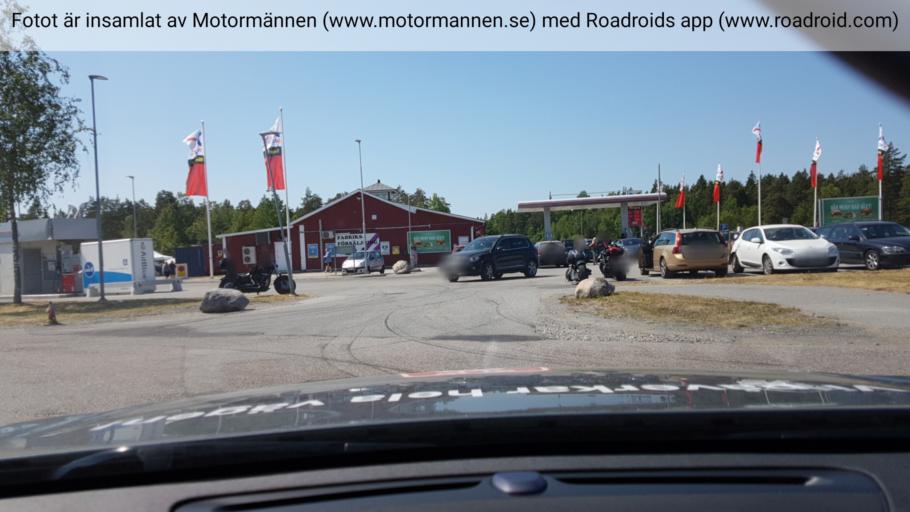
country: SE
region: Stockholm
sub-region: Norrtalje Kommun
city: Rimbo
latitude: 59.6348
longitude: 18.3318
